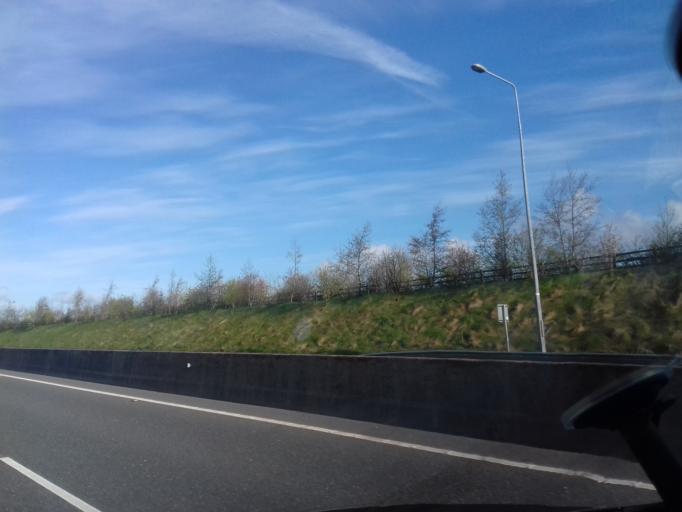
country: IE
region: Leinster
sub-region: An Mhi
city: Navan
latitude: 53.6745
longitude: -6.7835
